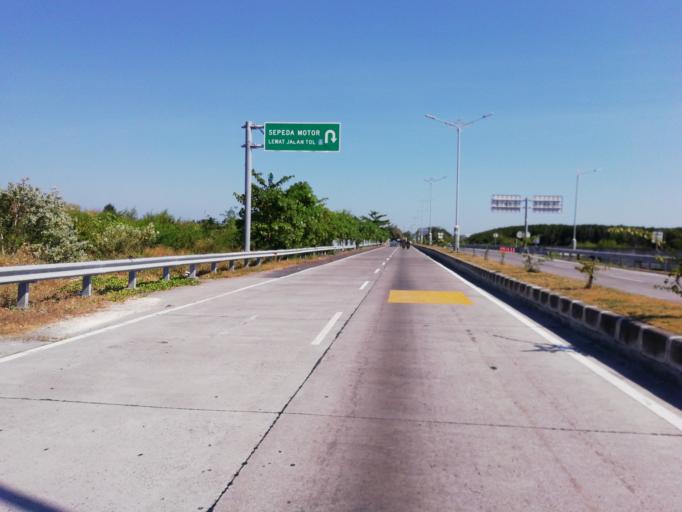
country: ID
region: Bali
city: Karyadharma
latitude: -8.7348
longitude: 115.2116
